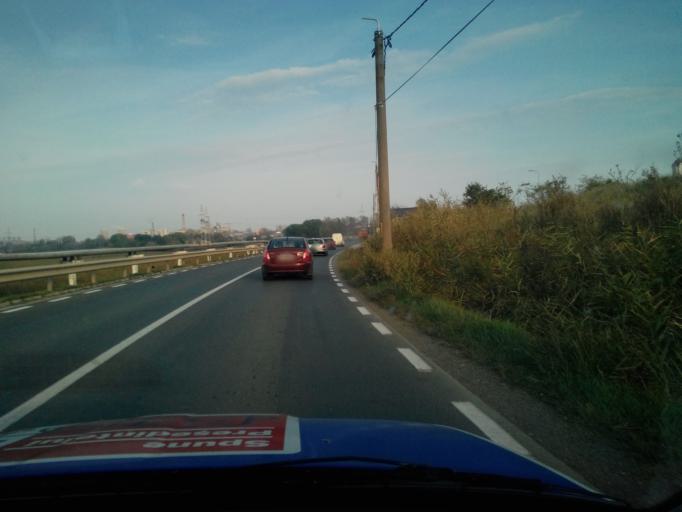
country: RO
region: Tulcea
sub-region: Comuna Somova
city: Mineri
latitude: 45.1722
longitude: 28.7458
